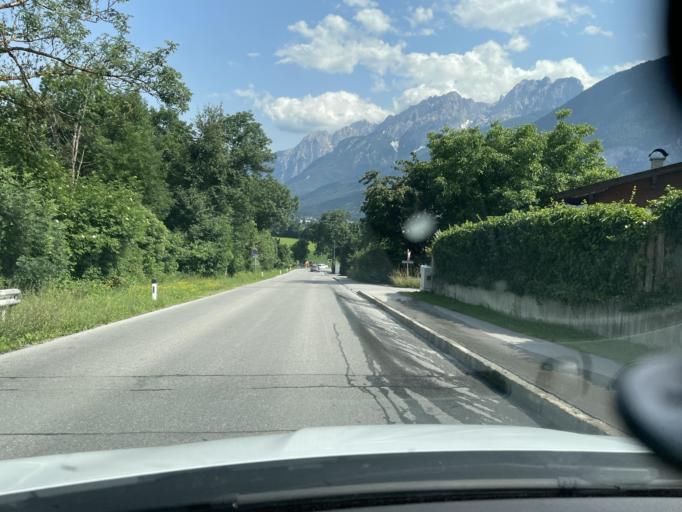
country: AT
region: Tyrol
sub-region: Politischer Bezirk Lienz
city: Lienz
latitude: 46.8398
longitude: 12.7767
